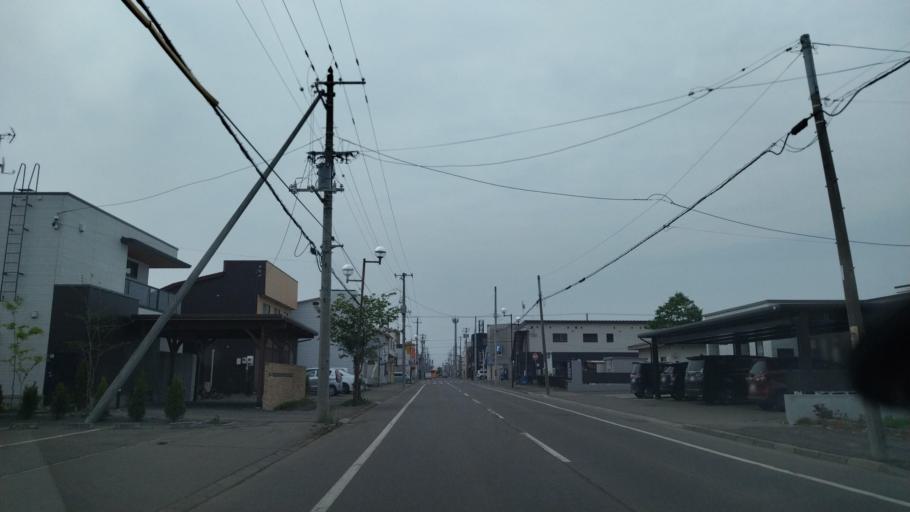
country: JP
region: Hokkaido
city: Obihiro
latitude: 42.9141
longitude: 143.0494
